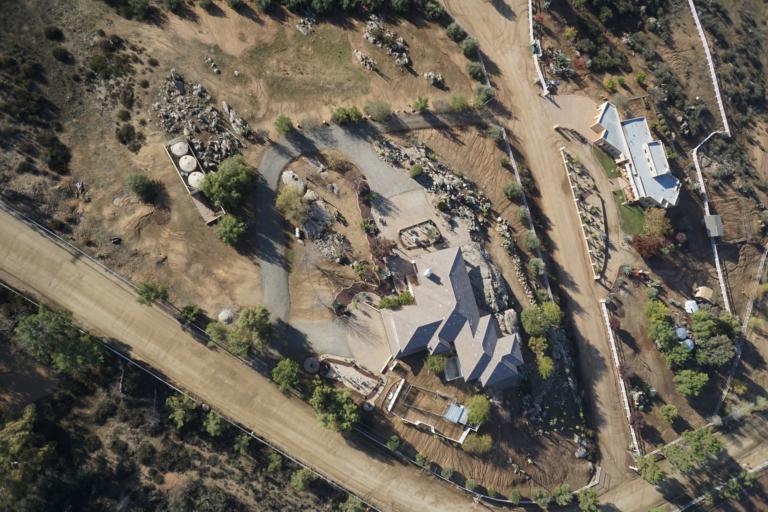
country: US
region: California
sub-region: Riverside County
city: East Hemet
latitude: 33.6115
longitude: -116.9387
